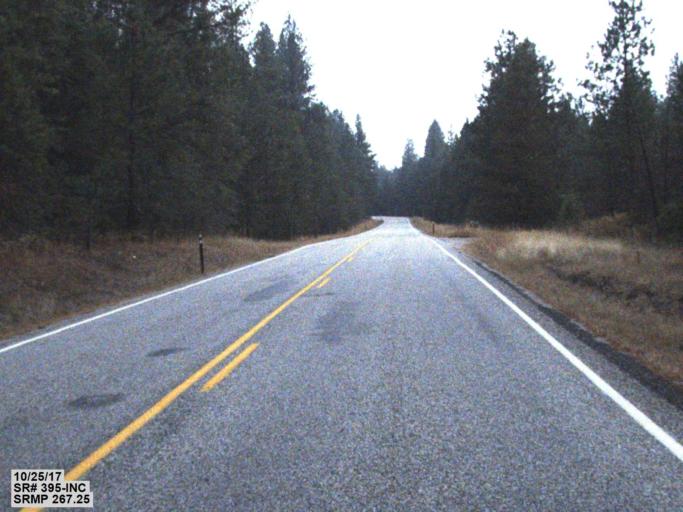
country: CA
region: British Columbia
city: Grand Forks
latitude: 48.9584
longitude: -118.2143
